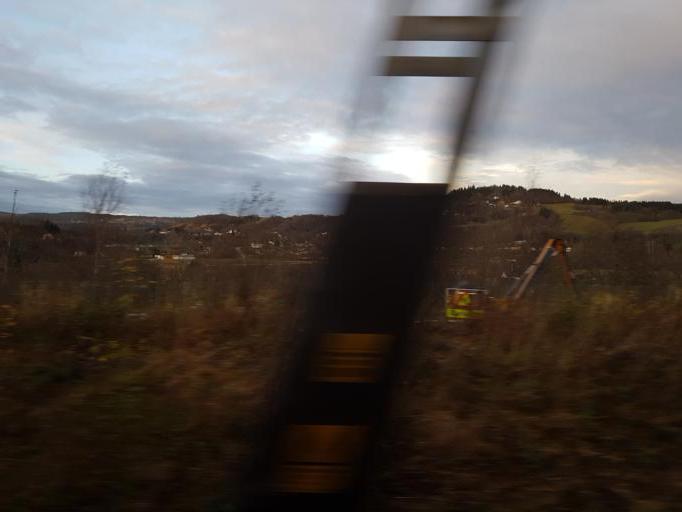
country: NO
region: Sor-Trondelag
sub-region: Melhus
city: Melhus
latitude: 63.2844
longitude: 10.2712
